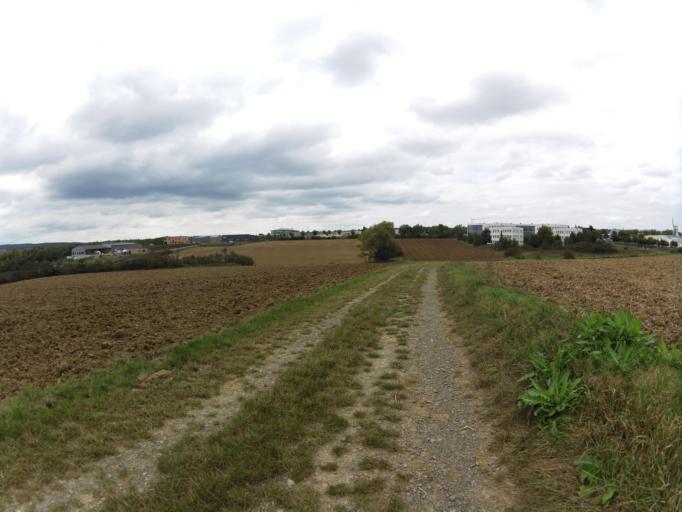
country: DE
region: Bavaria
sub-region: Regierungsbezirk Unterfranken
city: Eibelstadt
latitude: 49.7263
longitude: 9.9638
